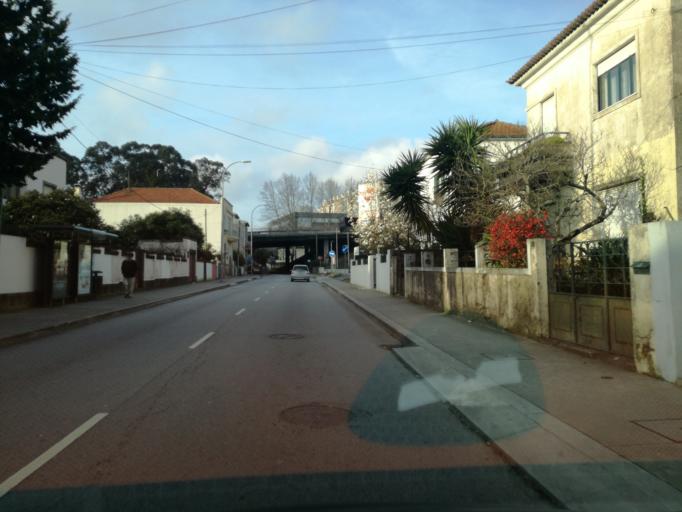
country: PT
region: Porto
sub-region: Porto
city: Porto
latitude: 41.1720
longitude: -8.6261
